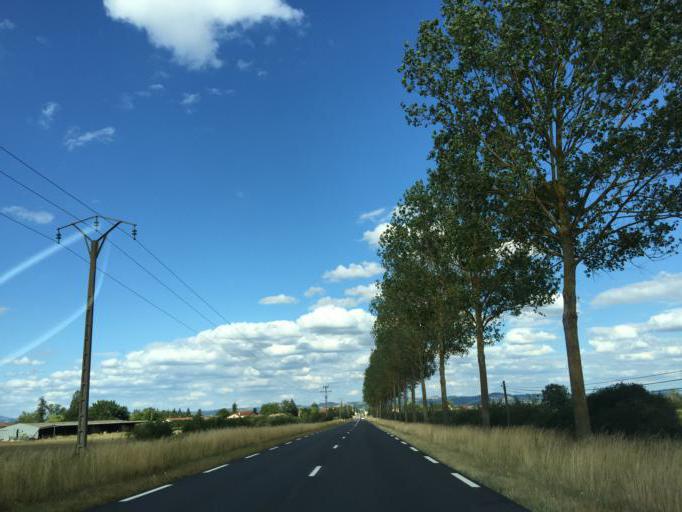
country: FR
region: Rhone-Alpes
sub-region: Departement de la Loire
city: Precieux
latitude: 45.6289
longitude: 4.1705
